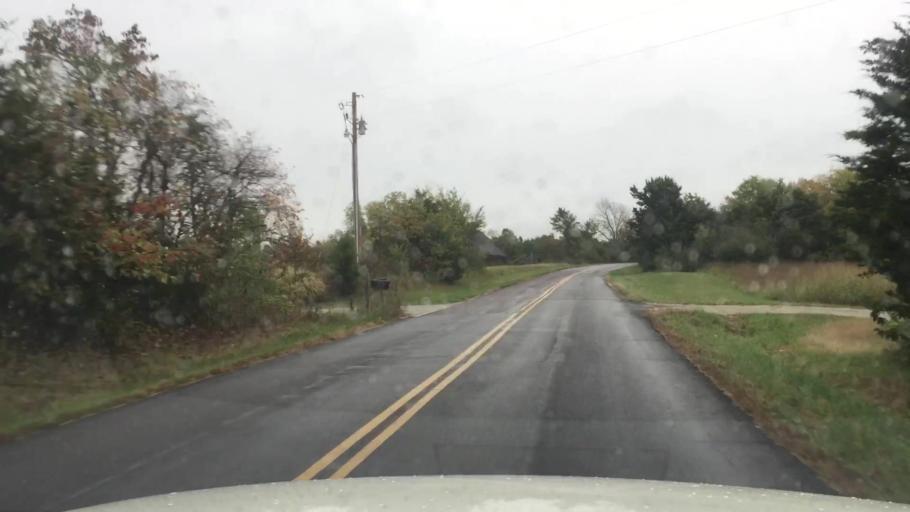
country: US
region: Missouri
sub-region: Boone County
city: Ashland
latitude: 38.7200
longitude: -92.2764
